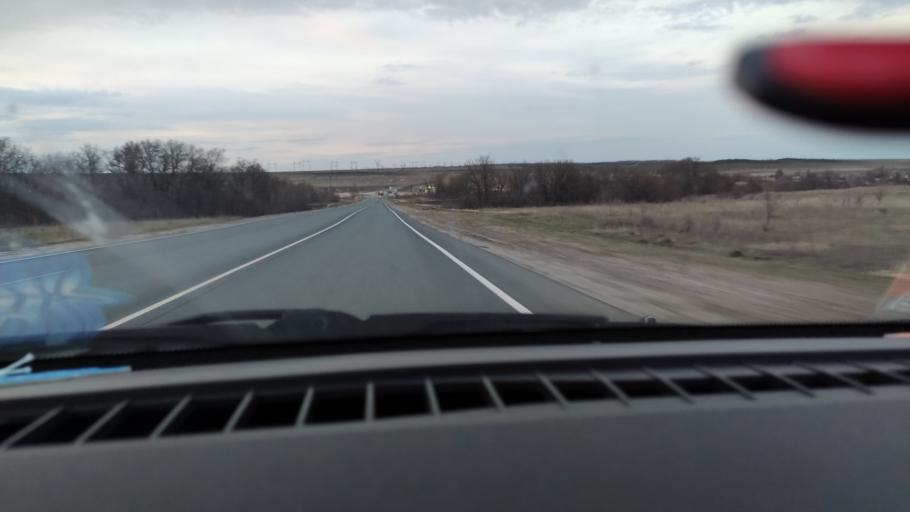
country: RU
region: Saratov
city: Sinodskoye
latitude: 51.9217
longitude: 46.5616
